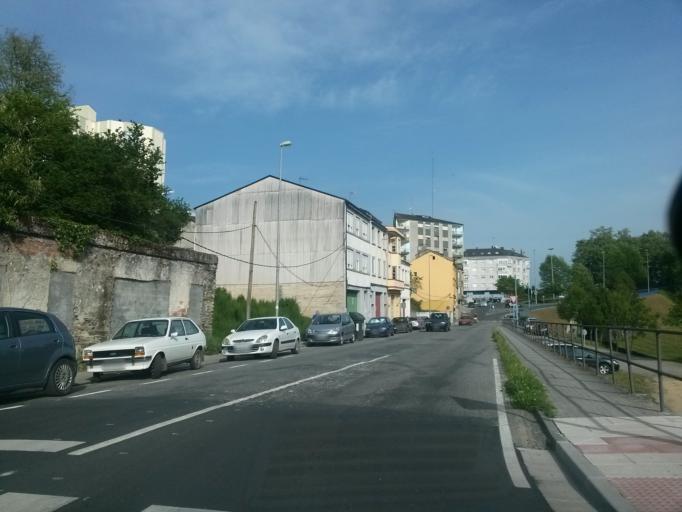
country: ES
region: Galicia
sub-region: Provincia de Lugo
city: Lugo
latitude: 43.0171
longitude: -7.5529
